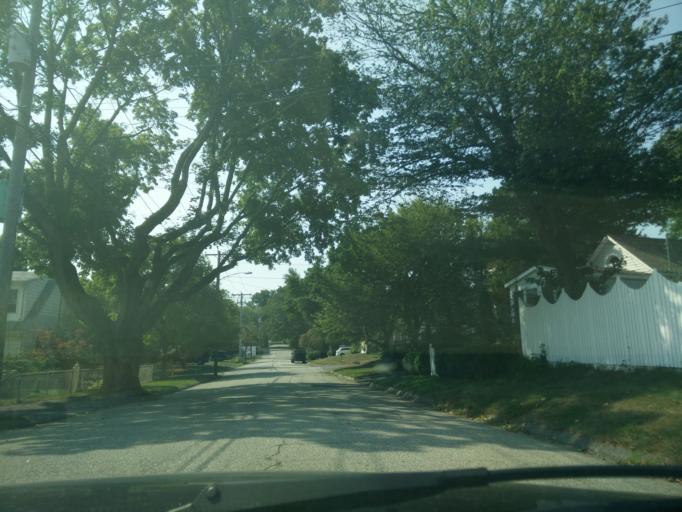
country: US
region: Connecticut
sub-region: Fairfield County
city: Bridgeport
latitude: 41.1811
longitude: -73.2338
